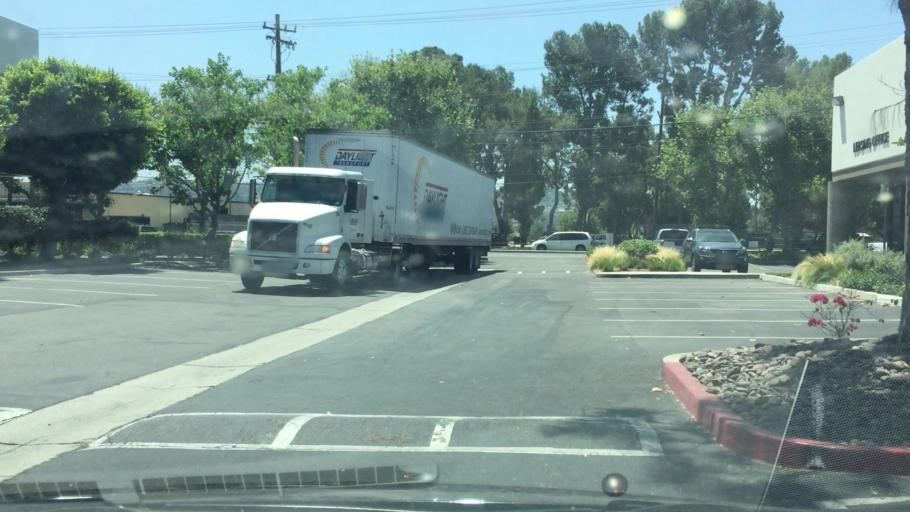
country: US
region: California
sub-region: Orange County
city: Yorba Linda
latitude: 33.8598
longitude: -117.8292
